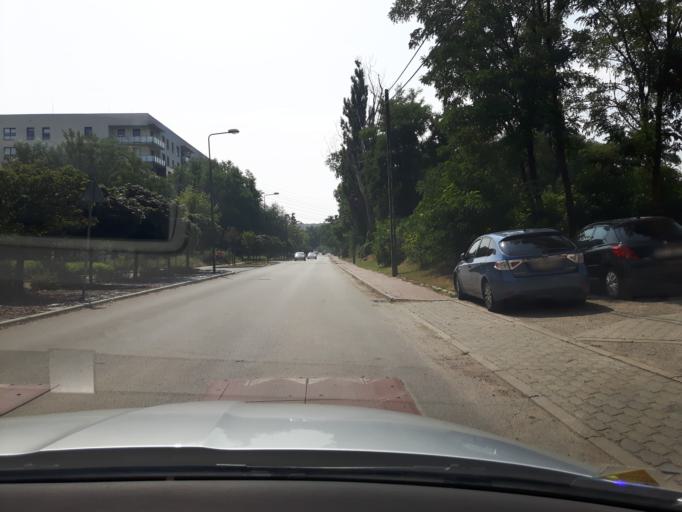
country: PL
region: Masovian Voivodeship
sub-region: Warszawa
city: Ochota
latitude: 52.2150
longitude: 20.9607
